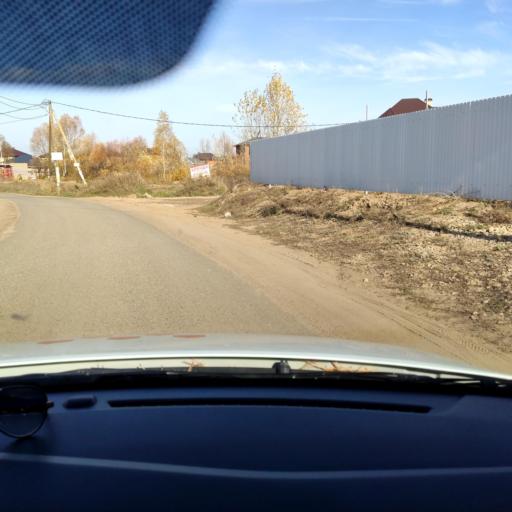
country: RU
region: Tatarstan
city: Vysokaya Gora
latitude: 55.7872
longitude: 49.2611
